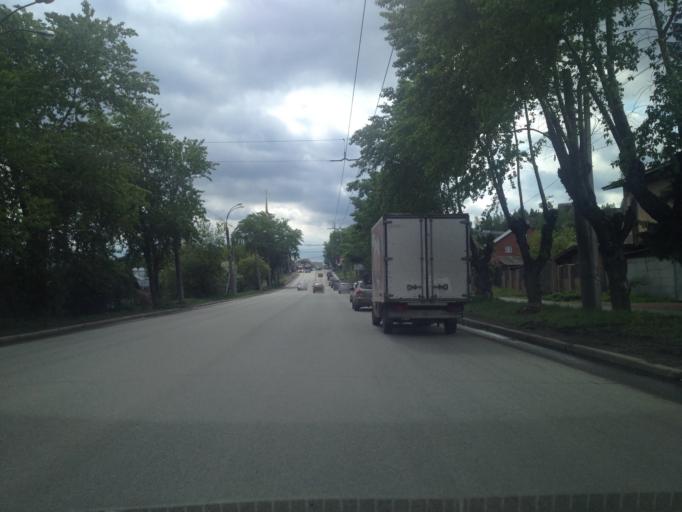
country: RU
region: Sverdlovsk
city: Istok
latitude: 56.7480
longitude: 60.6828
